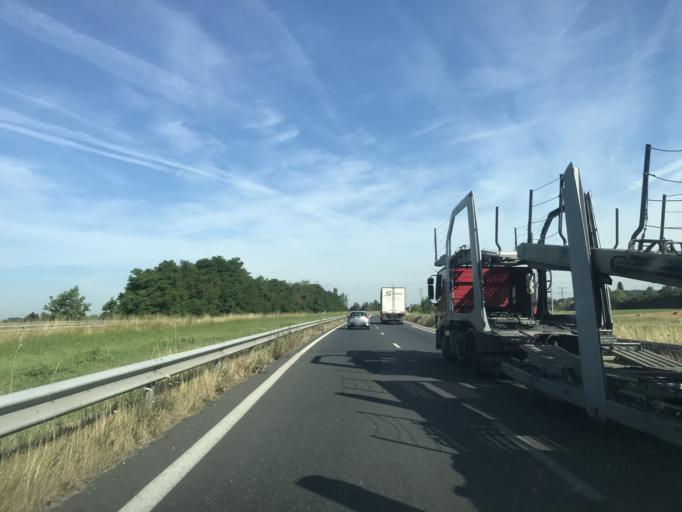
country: FR
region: Haute-Normandie
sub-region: Departement de la Seine-Maritime
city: La Vaupaliere
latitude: 49.4846
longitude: 1.0042
